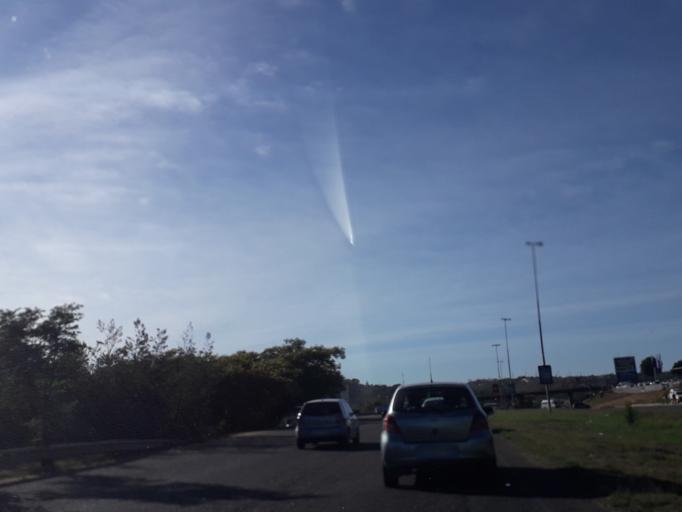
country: ZA
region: Gauteng
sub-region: City of Johannesburg Metropolitan Municipality
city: Roodepoort
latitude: -26.1432
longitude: 27.9211
